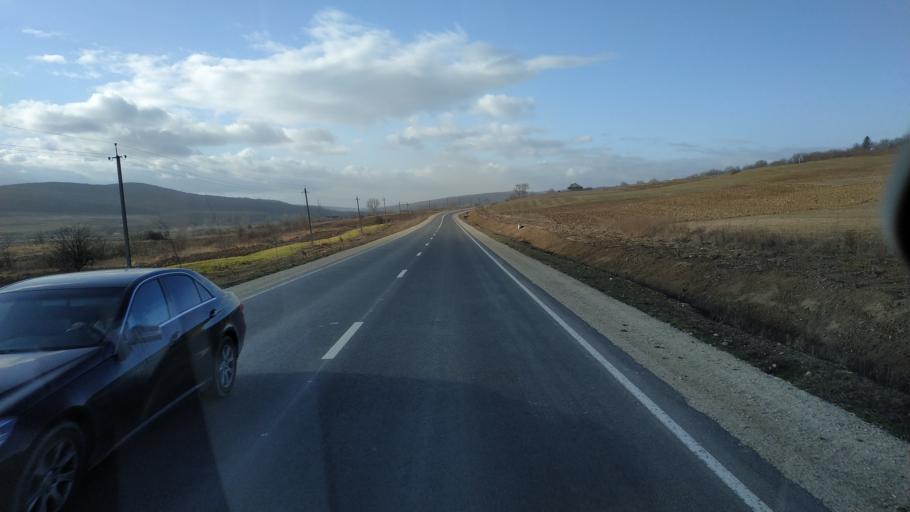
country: MD
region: Calarasi
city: Calarasi
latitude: 47.3116
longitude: 28.1223
